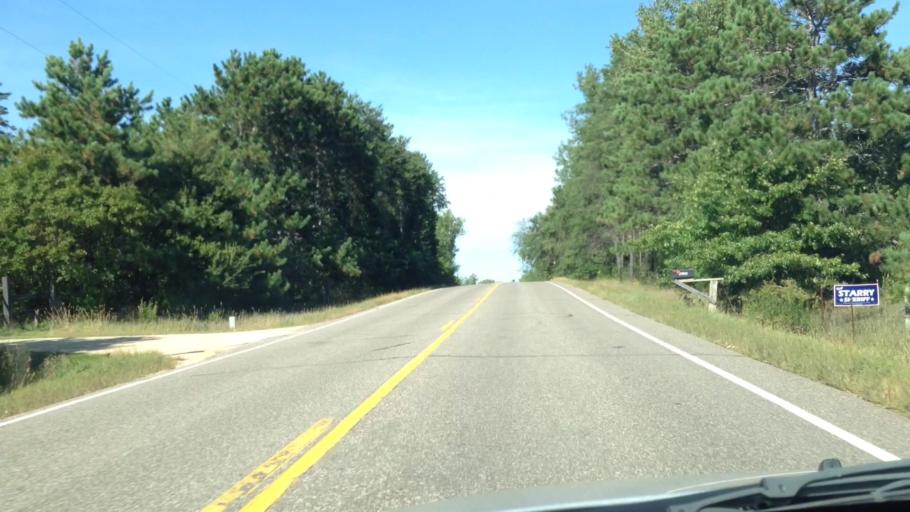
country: US
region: Minnesota
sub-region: Washington County
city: Stillwater
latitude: 45.1103
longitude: -92.8127
